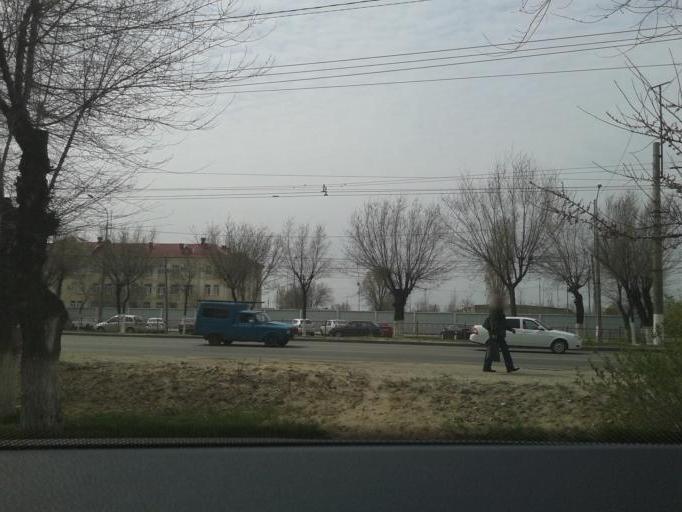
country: RU
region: Volgograd
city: Volgograd
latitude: 48.7341
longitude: 44.4958
